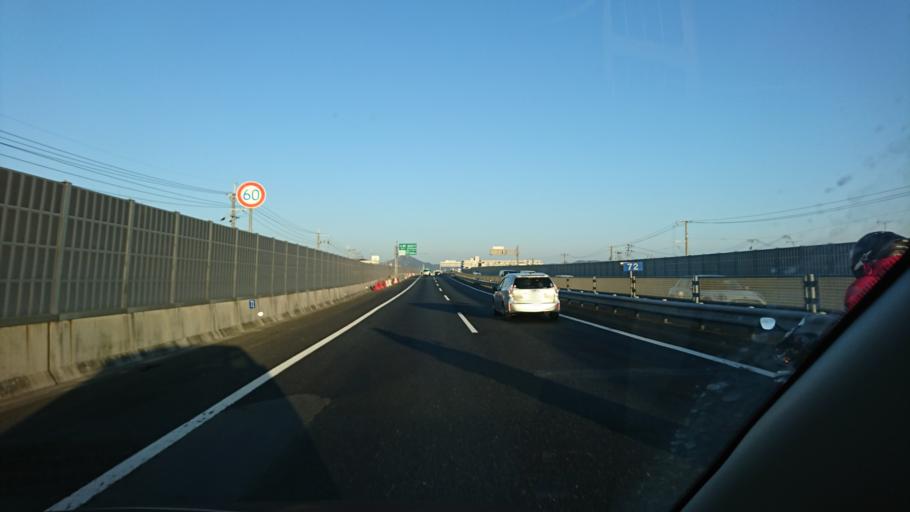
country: JP
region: Hyogo
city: Kakogawacho-honmachi
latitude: 34.7658
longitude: 134.8502
